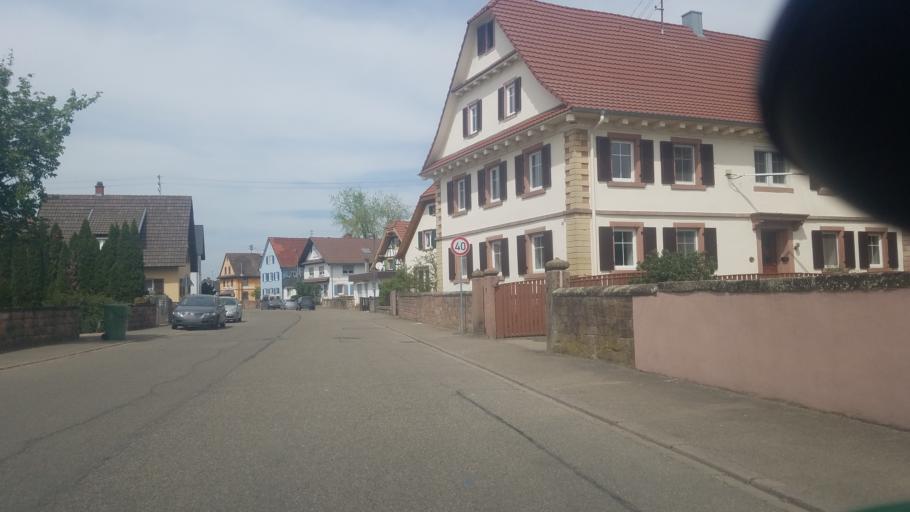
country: DE
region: Baden-Wuerttemberg
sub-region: Freiburg Region
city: Meissenheim
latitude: 48.4333
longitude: 7.8095
